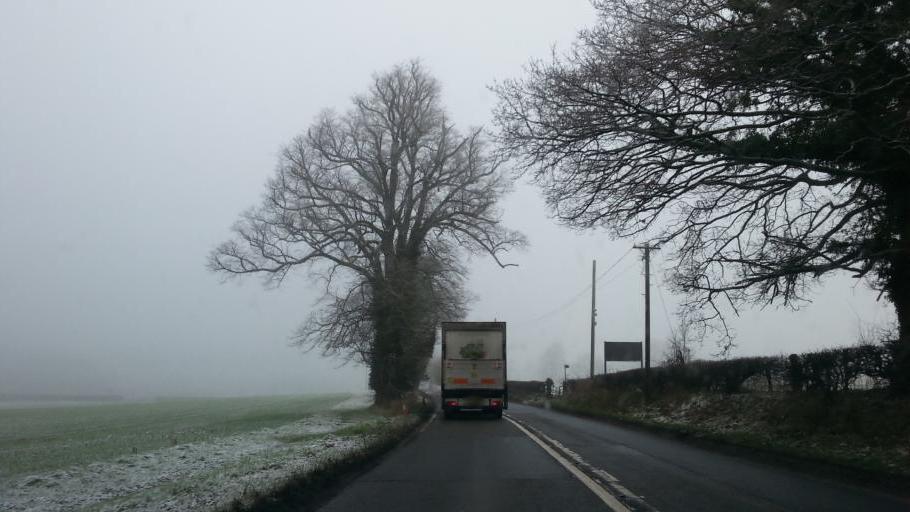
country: GB
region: England
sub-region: Cheshire East
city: Eaton
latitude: 53.1904
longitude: -2.2164
